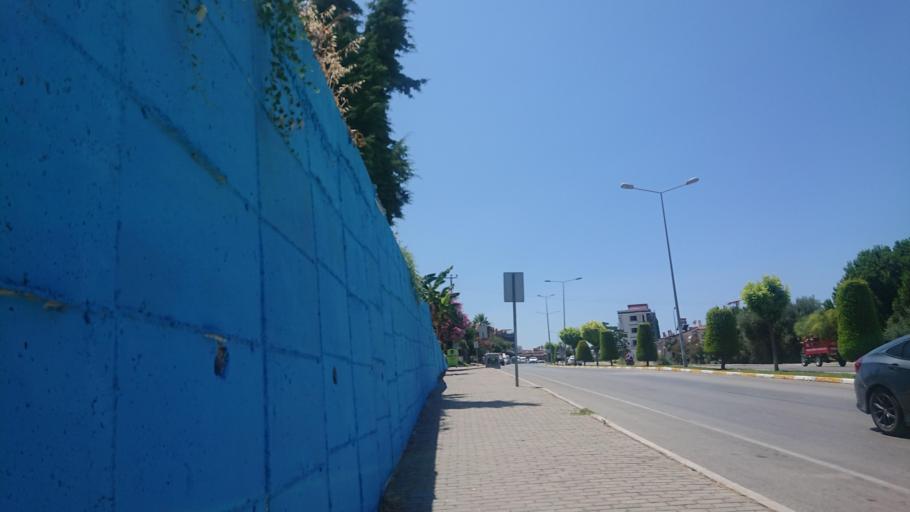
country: TR
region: Aydin
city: Kusadasi
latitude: 37.8672
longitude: 27.2684
